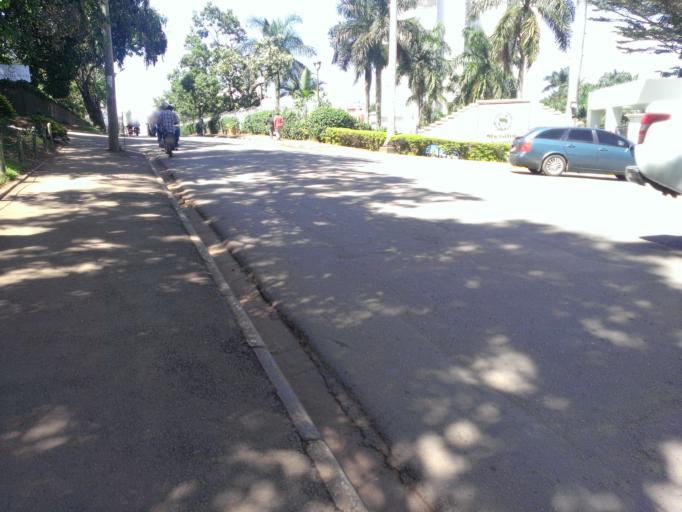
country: UG
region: Central Region
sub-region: Kampala District
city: Kampala
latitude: 0.3168
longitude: 32.5818
